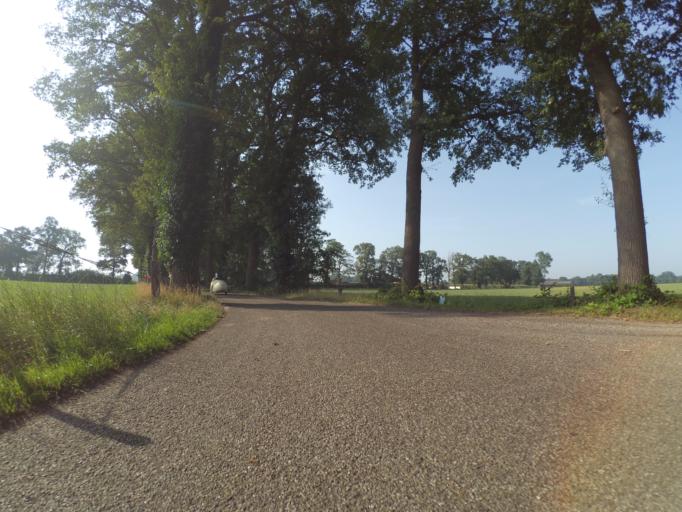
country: NL
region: Overijssel
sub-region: Gemeente Tubbergen
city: Tubbergen
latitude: 52.3466
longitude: 6.7933
